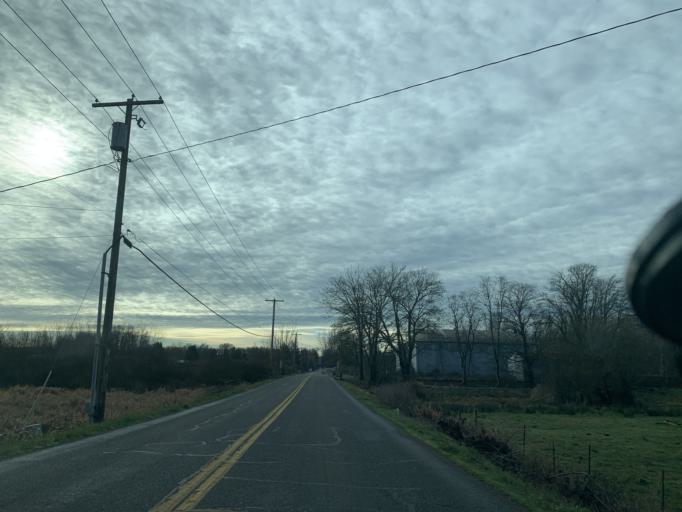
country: US
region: Washington
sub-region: Pierce County
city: Milton
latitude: 47.2189
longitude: -122.3206
